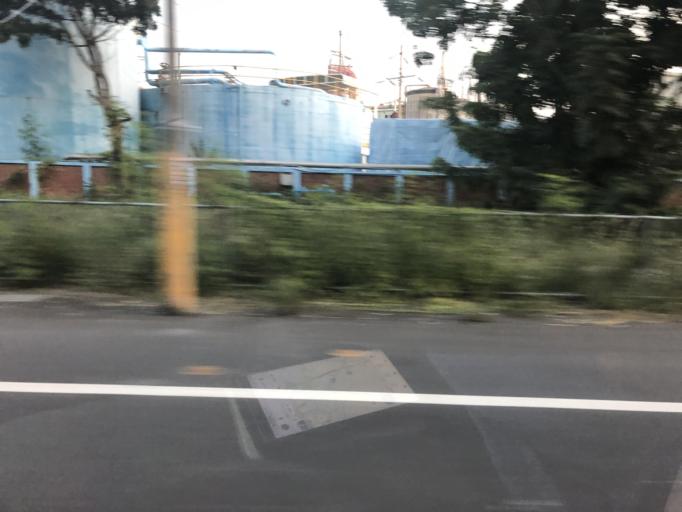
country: TW
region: Taiwan
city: Xinying
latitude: 23.2986
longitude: 120.2886
